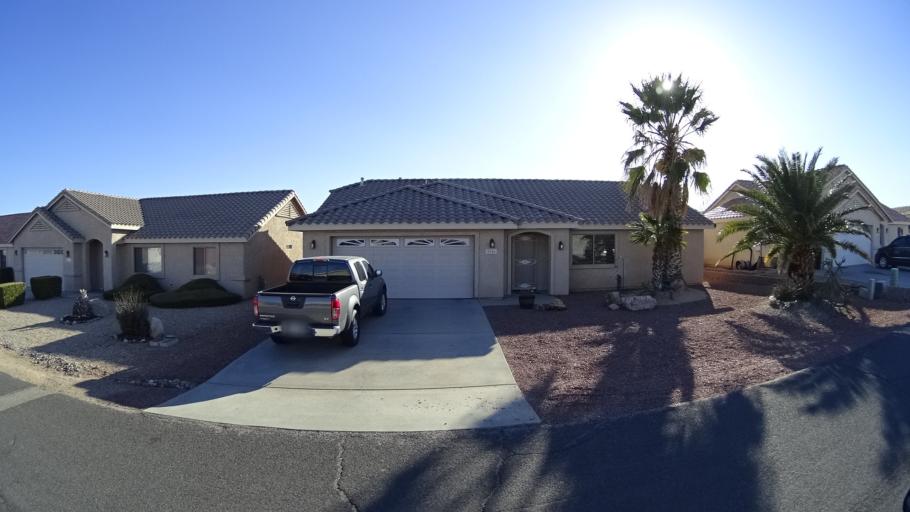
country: US
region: Arizona
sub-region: Mohave County
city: Kingman
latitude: 35.2126
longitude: -114.0085
